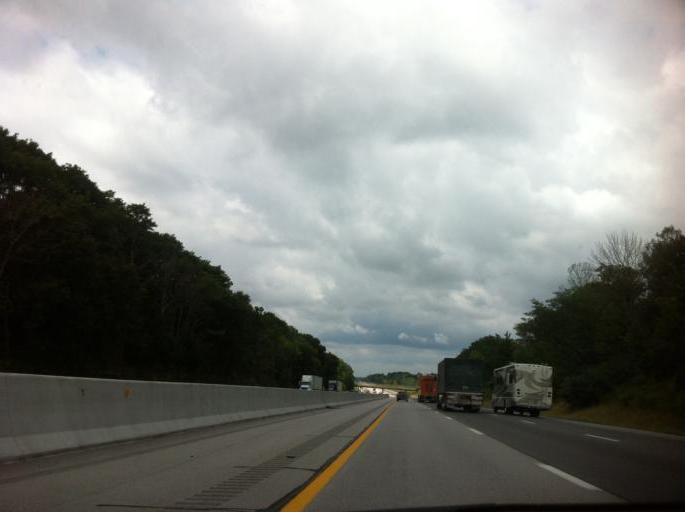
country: US
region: Ohio
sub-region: Summit County
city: Hudson
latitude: 41.2543
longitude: -81.4332
